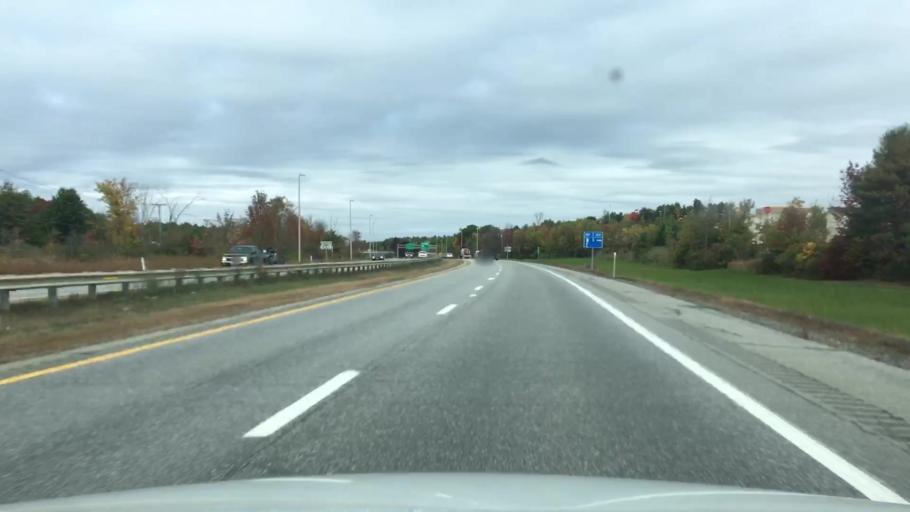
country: US
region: Maine
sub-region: Kennebec County
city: Hallowell
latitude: 44.3070
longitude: -69.8078
